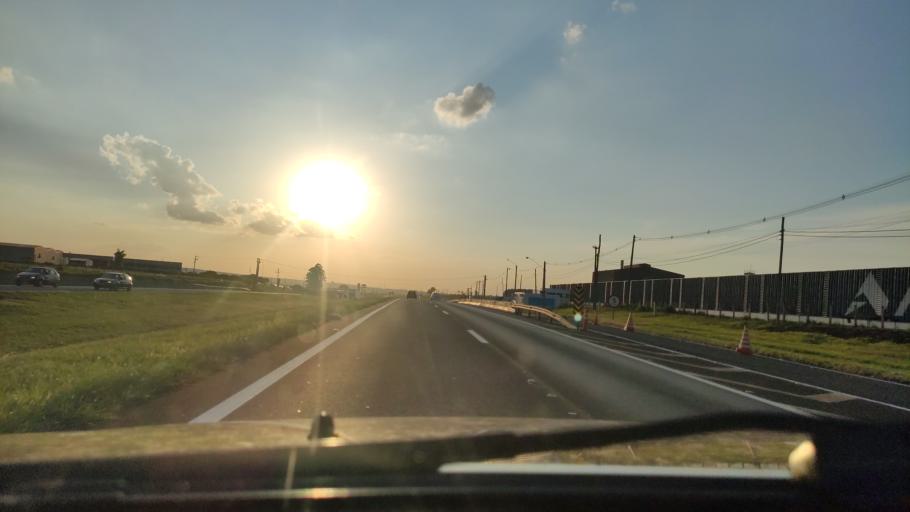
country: BR
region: Sao Paulo
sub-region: Cordeiropolis
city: Cordeiropolis
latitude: -22.4970
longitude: -47.4167
